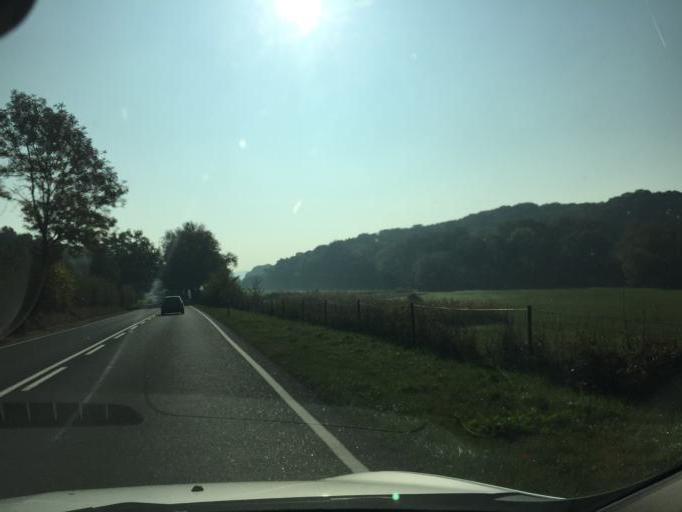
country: LU
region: Grevenmacher
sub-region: Canton de Remich
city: Waldbredimus
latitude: 49.5663
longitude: 6.2912
